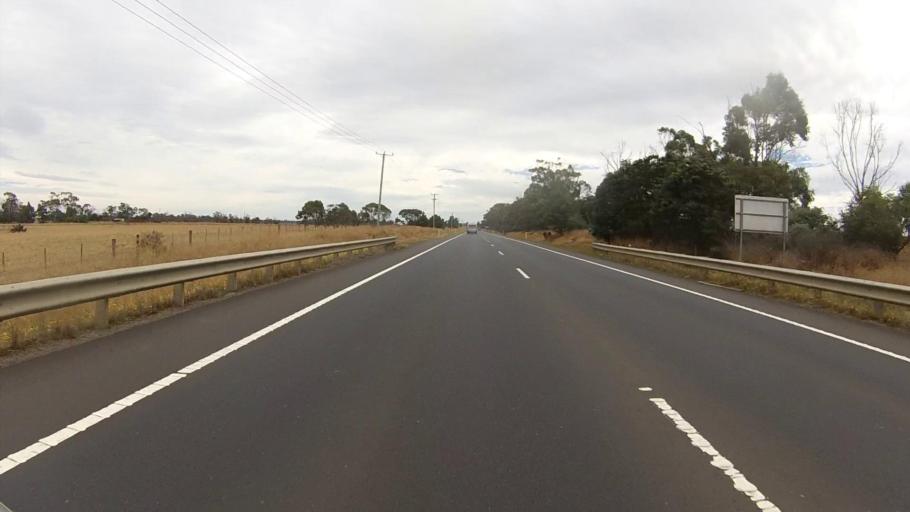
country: AU
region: Tasmania
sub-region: Northern Midlands
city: Evandale
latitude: -41.6906
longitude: 147.2818
